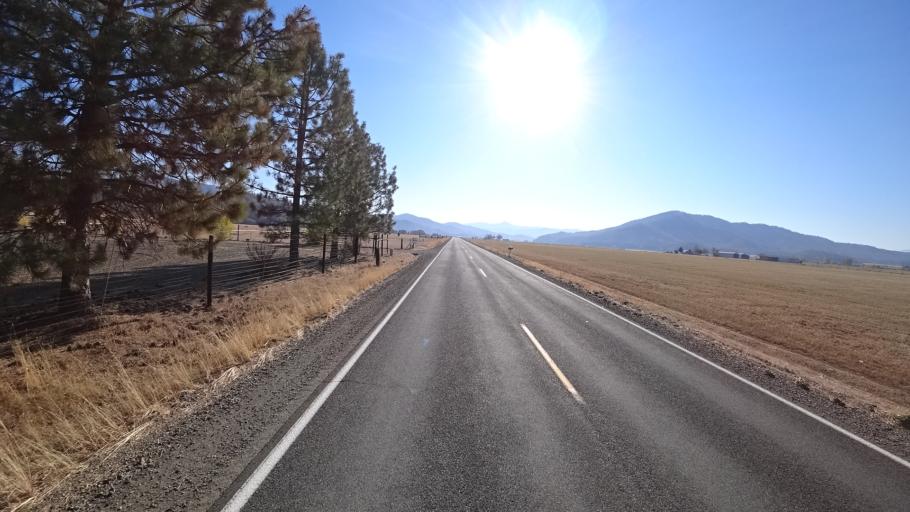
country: US
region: California
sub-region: Siskiyou County
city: Yreka
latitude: 41.6341
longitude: -122.9015
